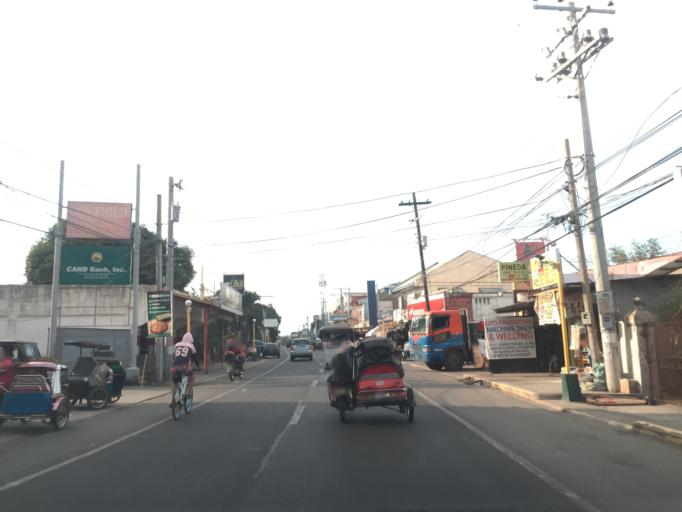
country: PH
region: Ilocos
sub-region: Province of Pangasinan
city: Bolingit
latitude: 15.9312
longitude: 120.3481
